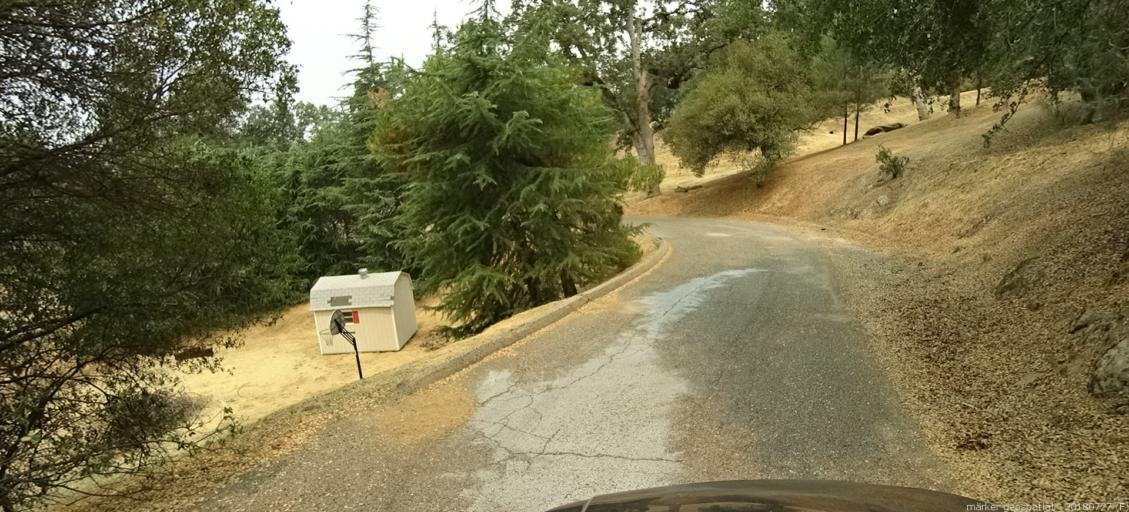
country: US
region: California
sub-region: Madera County
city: Oakhurst
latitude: 37.3322
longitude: -119.6209
